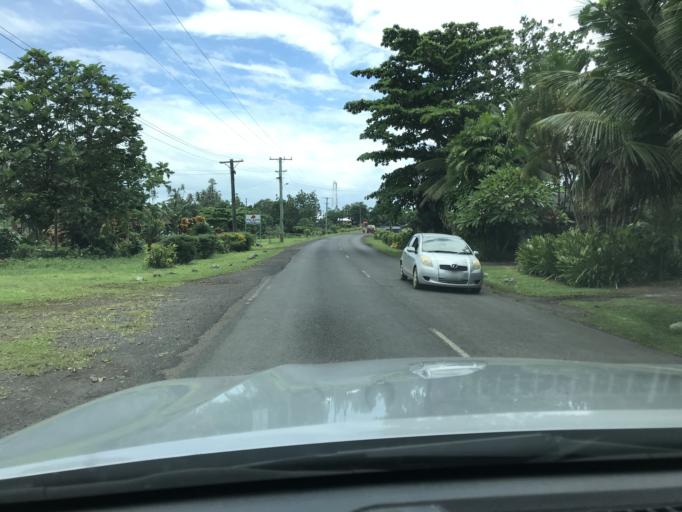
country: WS
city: Fasito`outa
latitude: -13.8051
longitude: -171.9176
